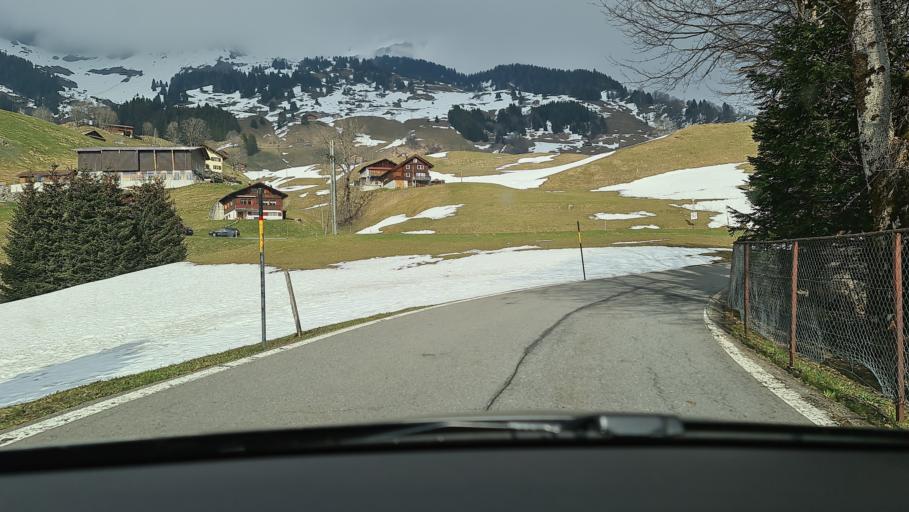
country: CH
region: Uri
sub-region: Uri
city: Burglen
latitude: 46.8717
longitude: 8.7585
